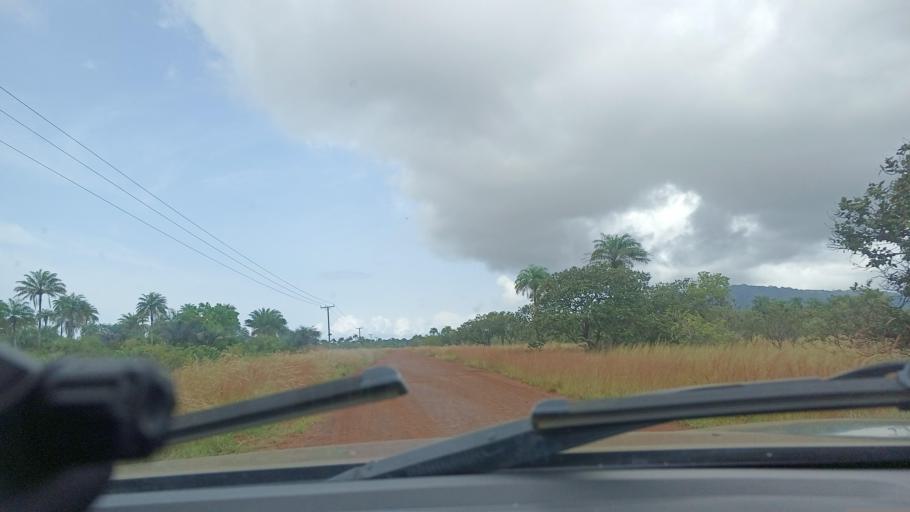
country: LR
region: Grand Cape Mount
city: Robertsport
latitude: 6.7031
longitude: -11.3130
